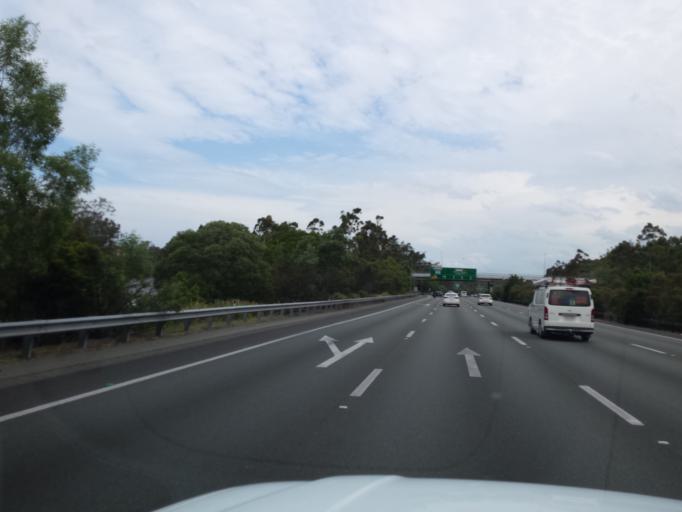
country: AU
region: Queensland
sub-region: Gold Coast
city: Nerang
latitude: -27.9487
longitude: 153.3414
